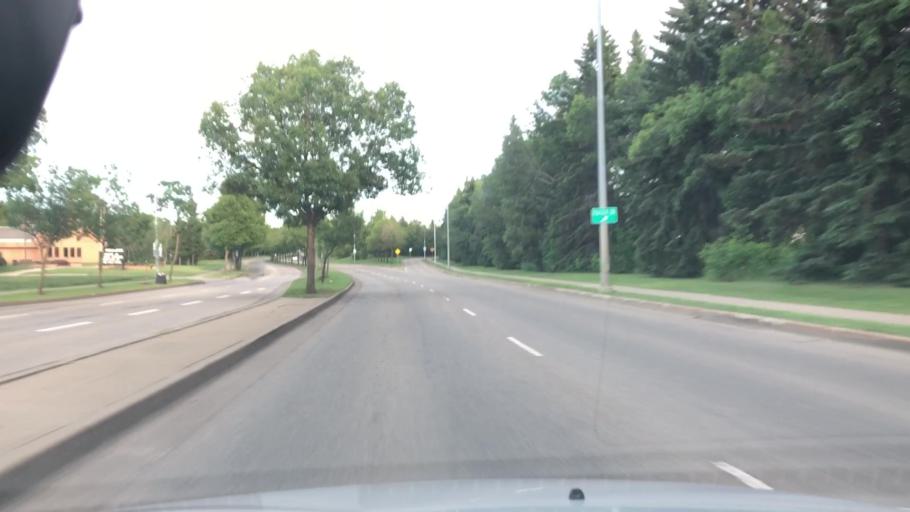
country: CA
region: Alberta
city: St. Albert
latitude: 53.6409
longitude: -113.6009
